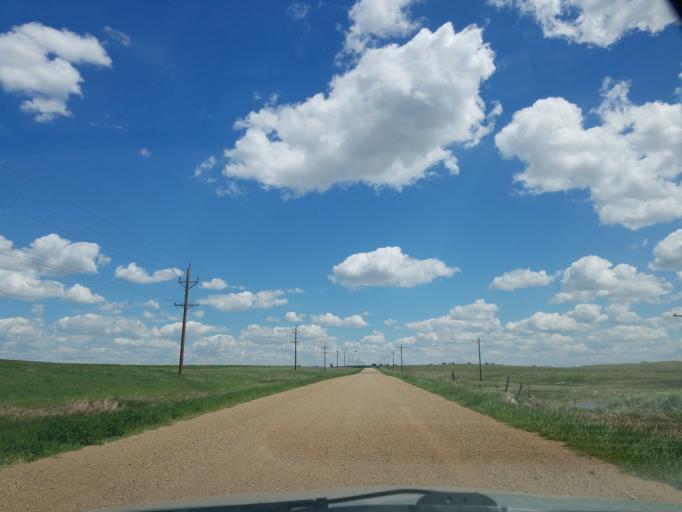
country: US
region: North Dakota
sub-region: McKenzie County
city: Watford City
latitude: 47.8195
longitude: -103.5716
